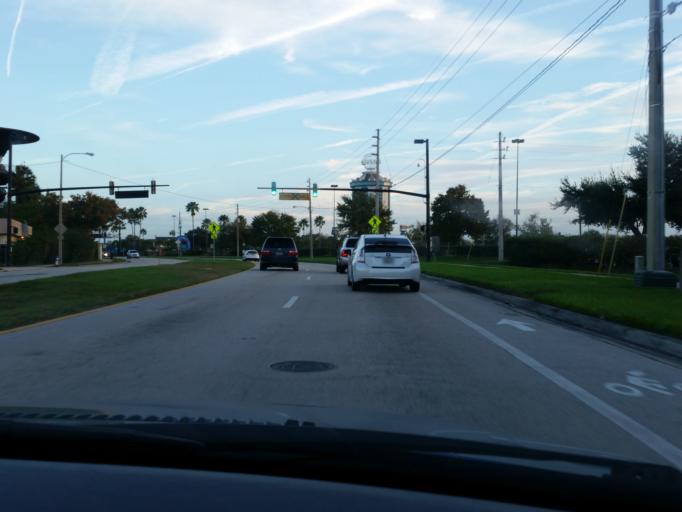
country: US
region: Florida
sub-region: Orange County
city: Tangelo Park
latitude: 28.4582
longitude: -81.4639
